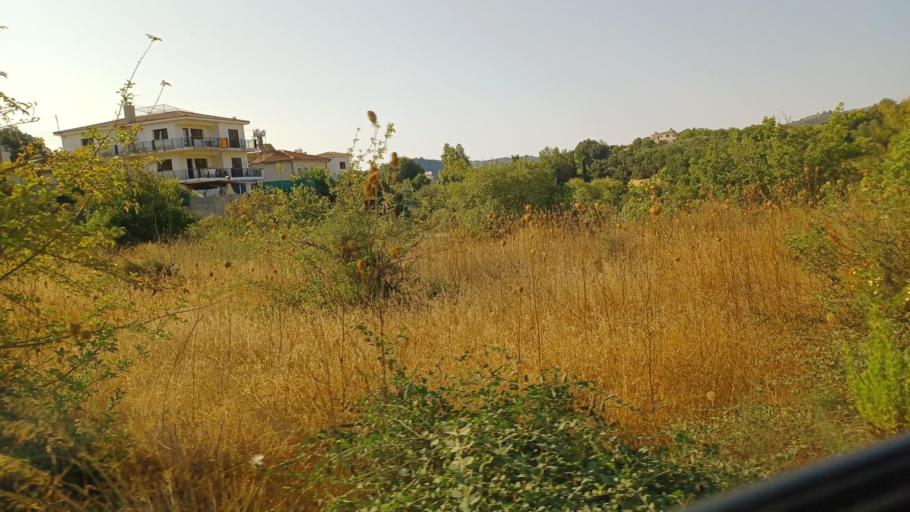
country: CY
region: Pafos
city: Tala
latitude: 34.8874
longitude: 32.4768
